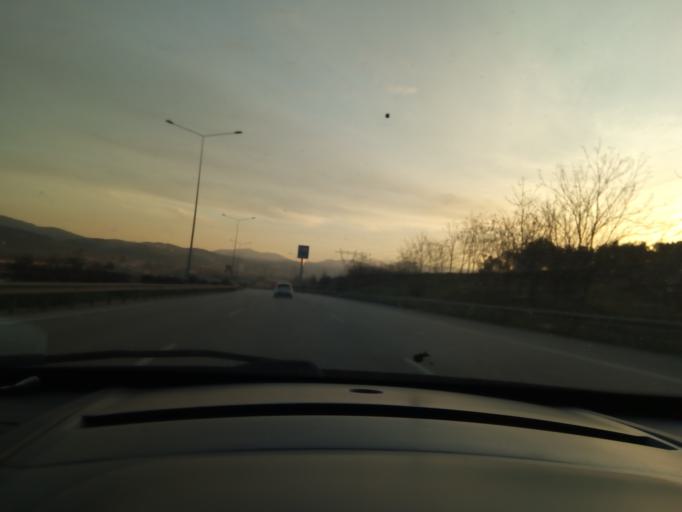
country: TR
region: Bursa
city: Niluefer
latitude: 40.2786
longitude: 28.9876
